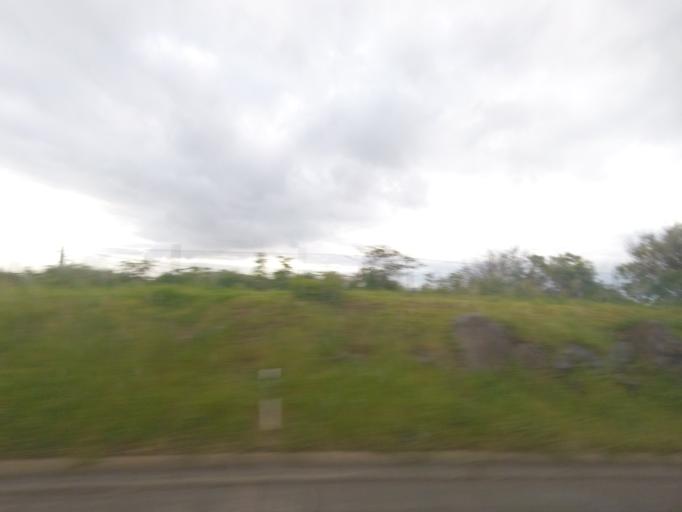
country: PT
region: Madeira
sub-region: Santa Cruz
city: Santa Cruz
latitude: 32.6718
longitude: -16.8033
